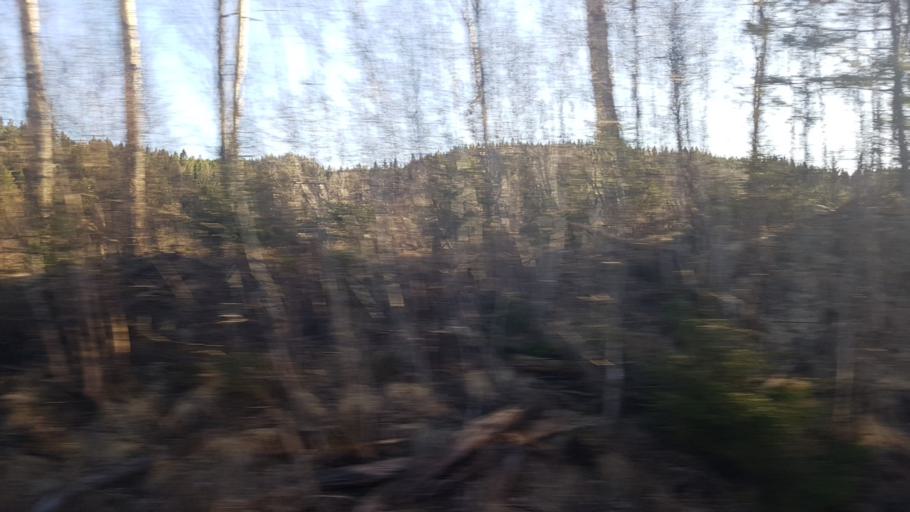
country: NO
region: Nord-Trondelag
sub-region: Levanger
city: Skogn
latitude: 63.6424
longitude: 11.0784
